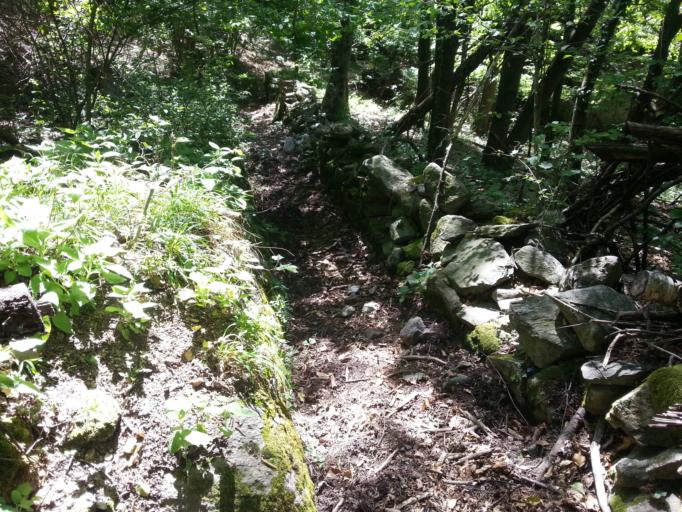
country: IT
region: Lombardy
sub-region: Provincia di Como
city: Codogna-Cardano
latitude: 46.0390
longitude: 9.2157
